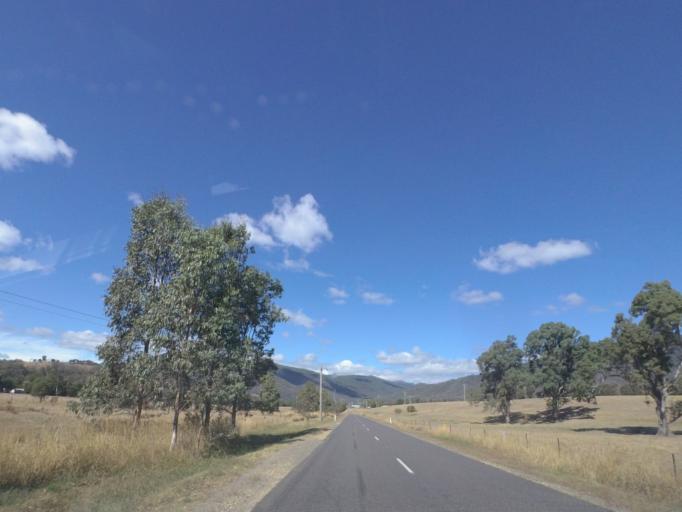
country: AU
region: Victoria
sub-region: Murrindindi
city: Alexandra
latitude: -37.2894
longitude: 145.8100
